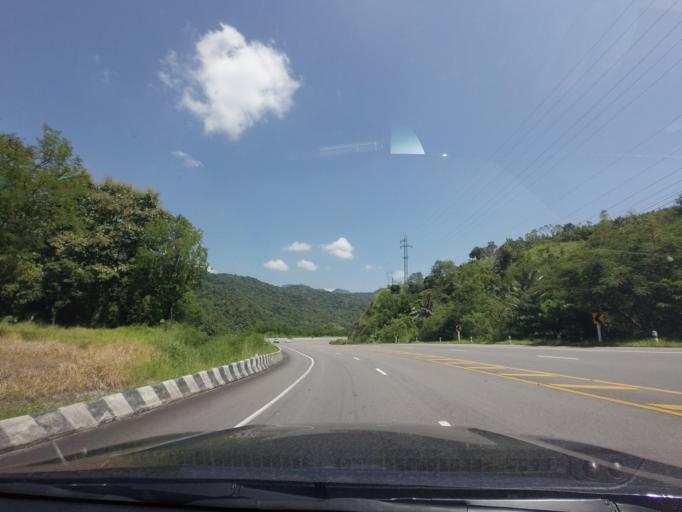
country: TH
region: Phetchabun
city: Lom Sak
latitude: 16.7800
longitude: 101.0998
